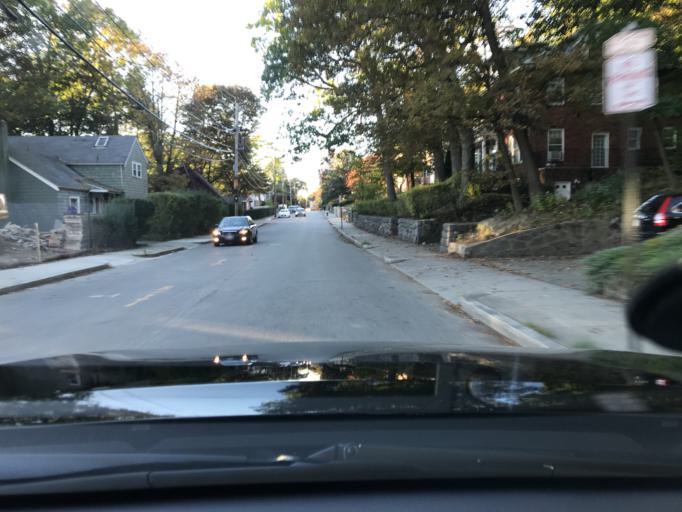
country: US
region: Massachusetts
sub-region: Norfolk County
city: Brookline
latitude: 42.3337
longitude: -71.1344
